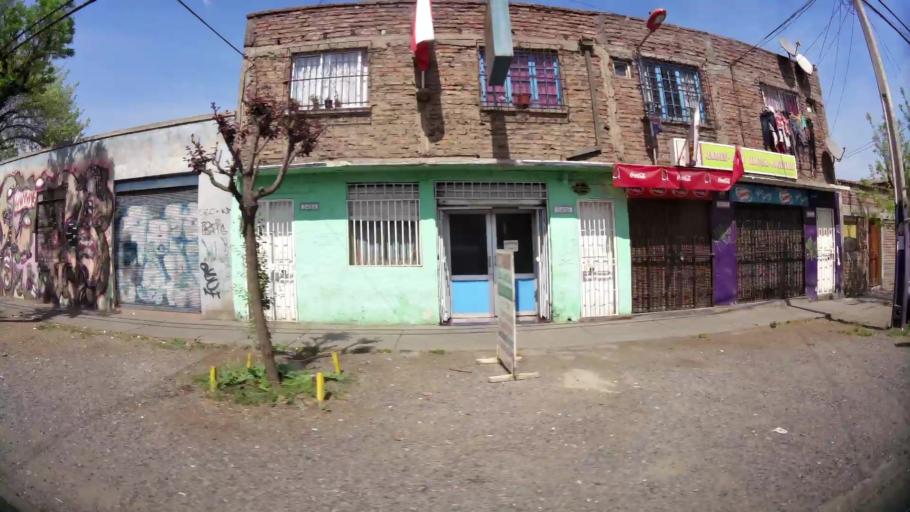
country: CL
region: Santiago Metropolitan
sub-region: Provincia de Santiago
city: Lo Prado
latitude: -33.4276
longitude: -70.7092
